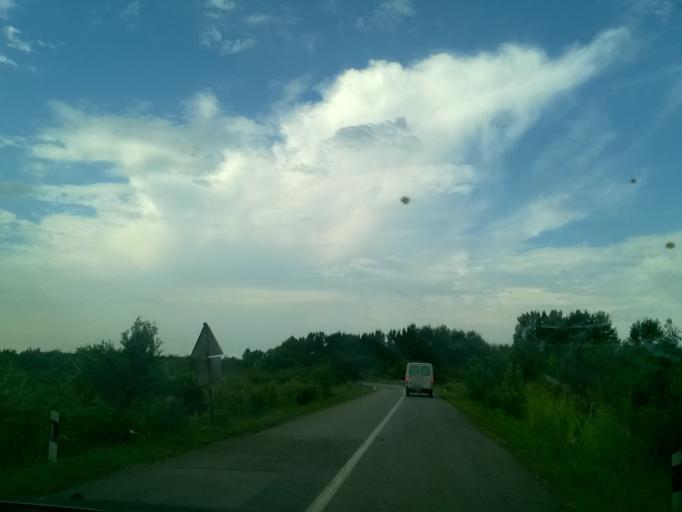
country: RS
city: Tomasevac
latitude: 45.2506
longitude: 20.6059
